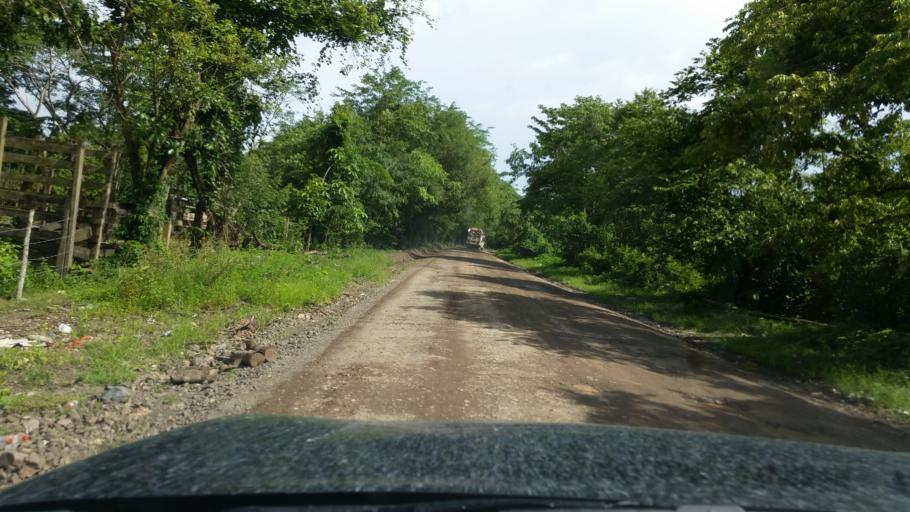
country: NI
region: Atlantico Norte (RAAN)
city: Siuna
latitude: 13.6844
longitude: -84.7898
